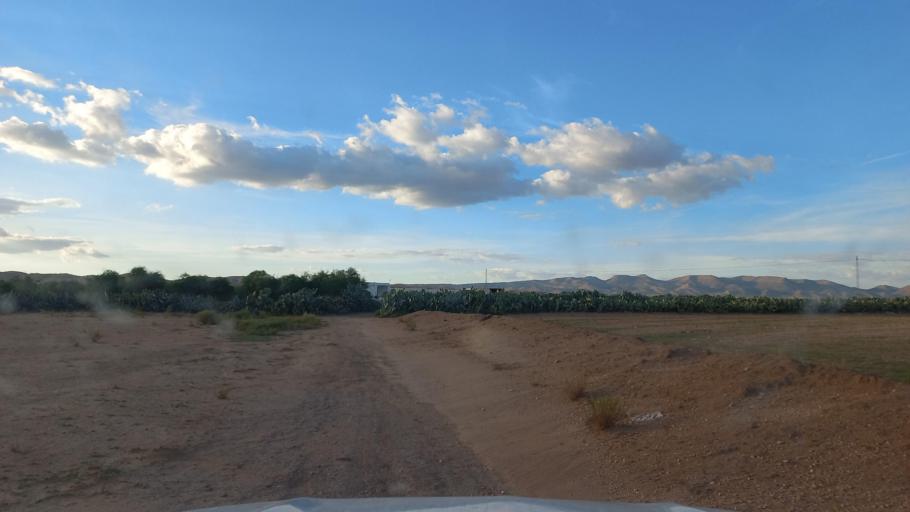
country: TN
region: Al Qasrayn
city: Sbiba
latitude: 35.3544
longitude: 9.0313
